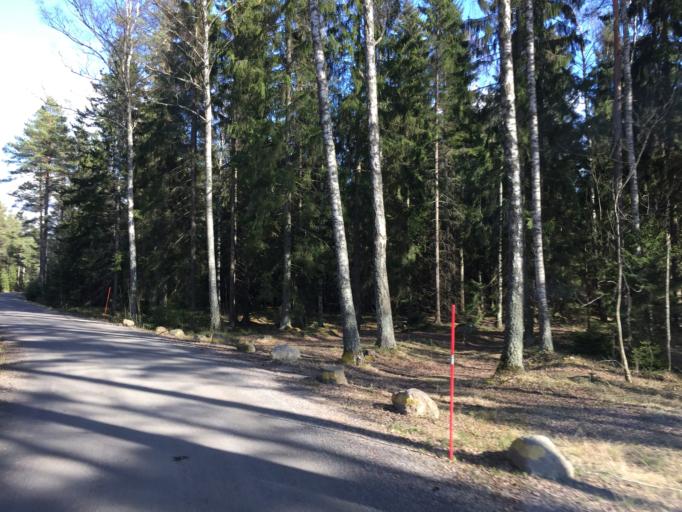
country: SE
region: Stockholm
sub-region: Sodertalje Kommun
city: Soedertaelje
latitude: 59.2352
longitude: 17.5385
